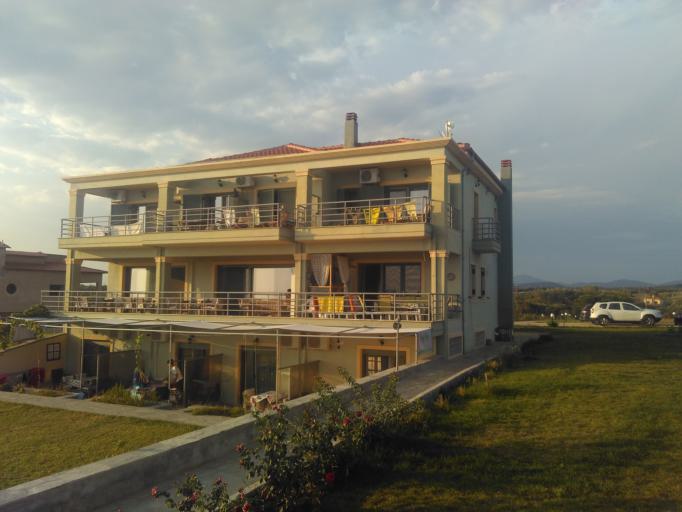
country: GR
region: East Macedonia and Thrace
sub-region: Nomos Rodopis
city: Xylagani
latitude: 40.8862
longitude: 25.4889
